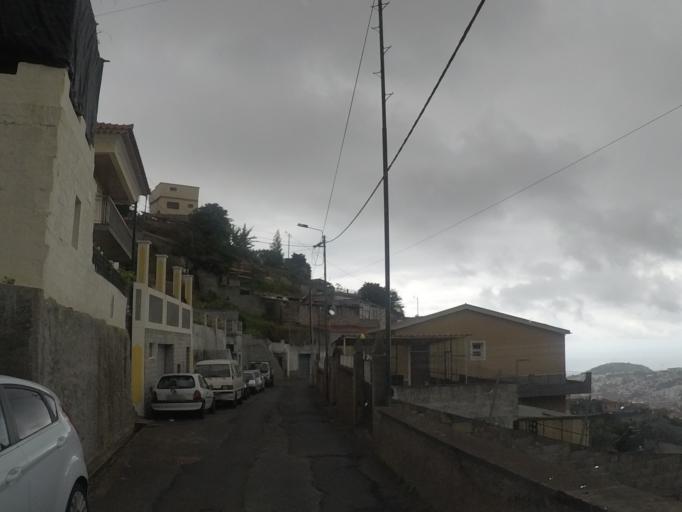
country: PT
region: Madeira
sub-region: Funchal
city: Nossa Senhora do Monte
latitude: 32.6725
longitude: -16.9137
